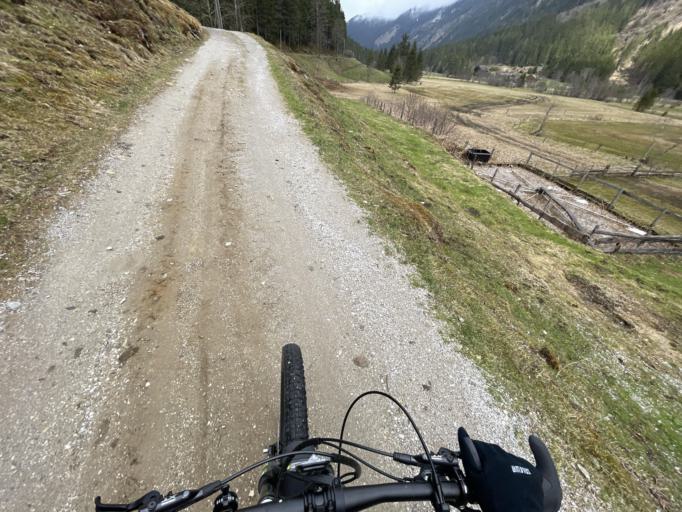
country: AT
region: Styria
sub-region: Politischer Bezirk Liezen
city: Schladming
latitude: 47.3378
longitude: 13.7384
